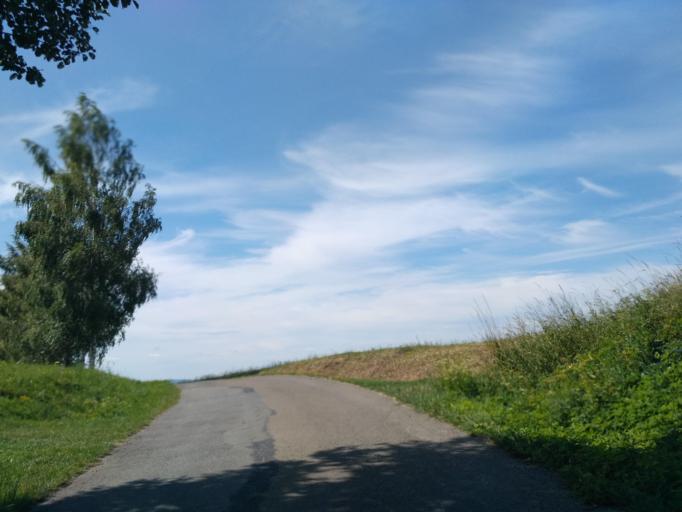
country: PL
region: Subcarpathian Voivodeship
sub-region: Powiat krosnienski
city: Korczyna
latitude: 49.7155
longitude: 21.8294
